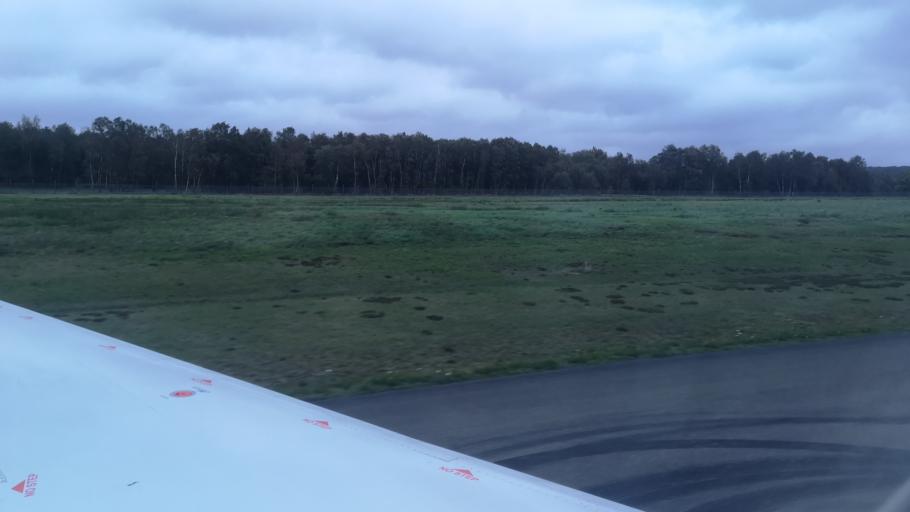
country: DK
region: South Denmark
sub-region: Billund Kommune
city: Billund
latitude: 55.7429
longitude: 9.1799
